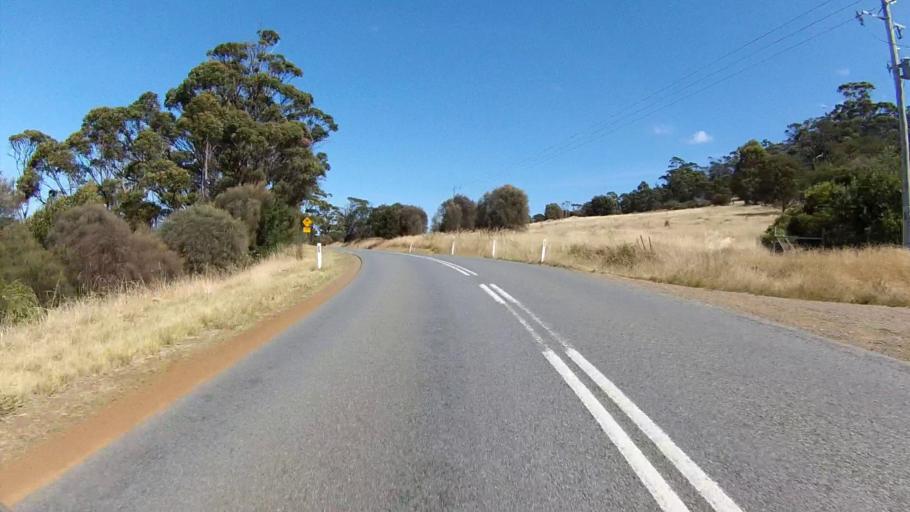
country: AU
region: Tasmania
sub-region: Sorell
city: Sorell
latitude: -42.2341
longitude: 148.0170
